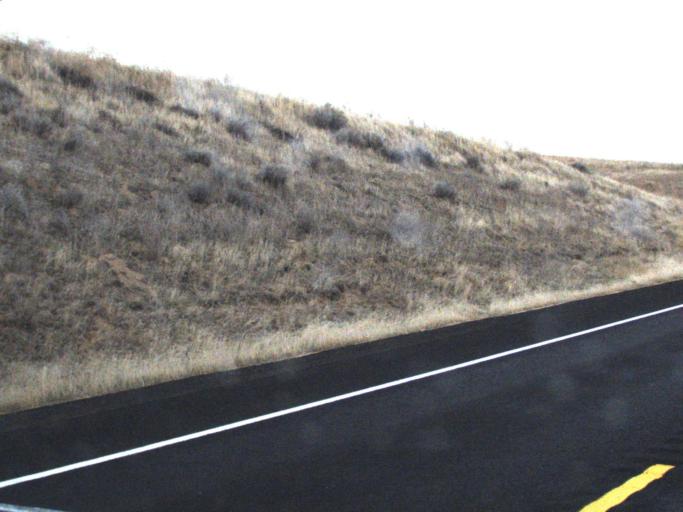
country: US
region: Washington
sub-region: Garfield County
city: Pomeroy
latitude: 46.8042
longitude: -117.7757
